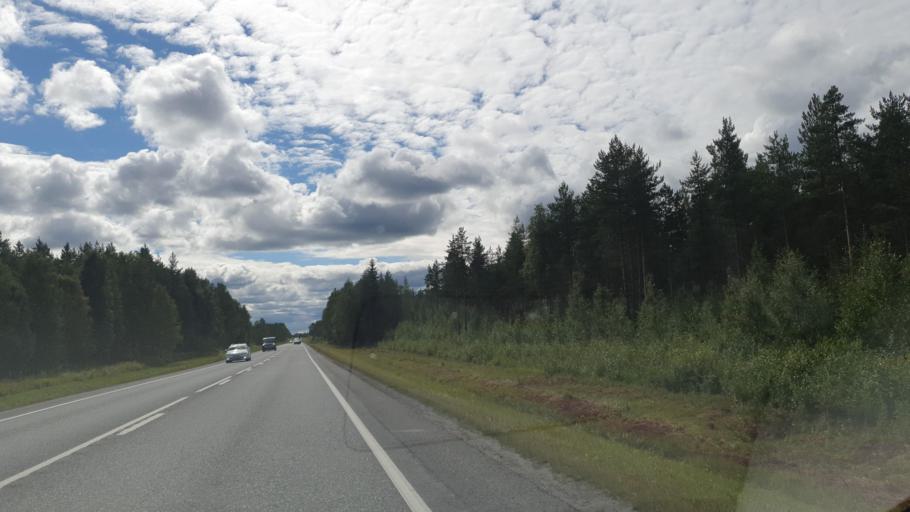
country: FI
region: Kainuu
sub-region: Kajaani
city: Kajaani
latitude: 64.1364
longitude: 27.4903
